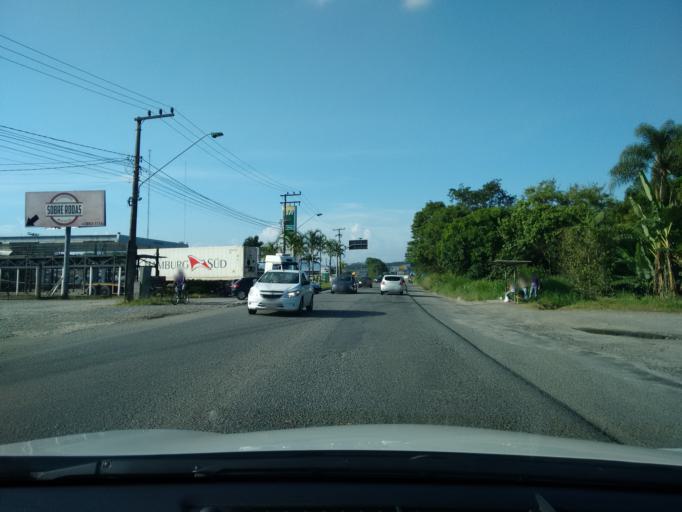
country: BR
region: Santa Catarina
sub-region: Blumenau
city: Blumenau
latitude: -26.8601
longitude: -49.0861
